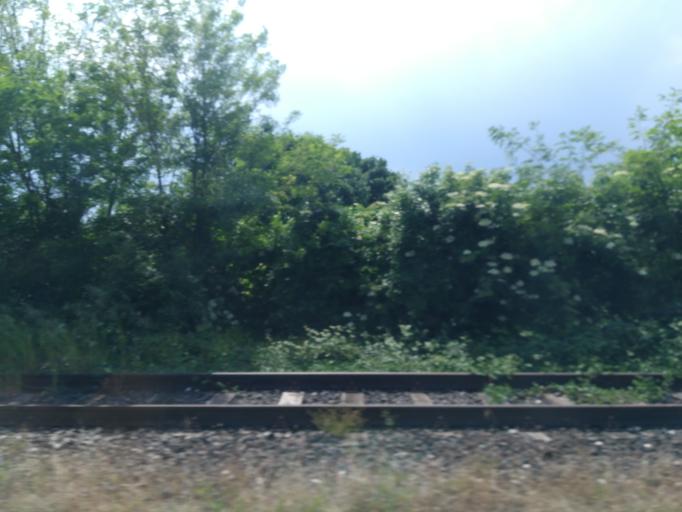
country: IT
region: Veneto
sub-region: Provincia di Vicenza
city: Thiene
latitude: 45.6981
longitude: 11.4783
